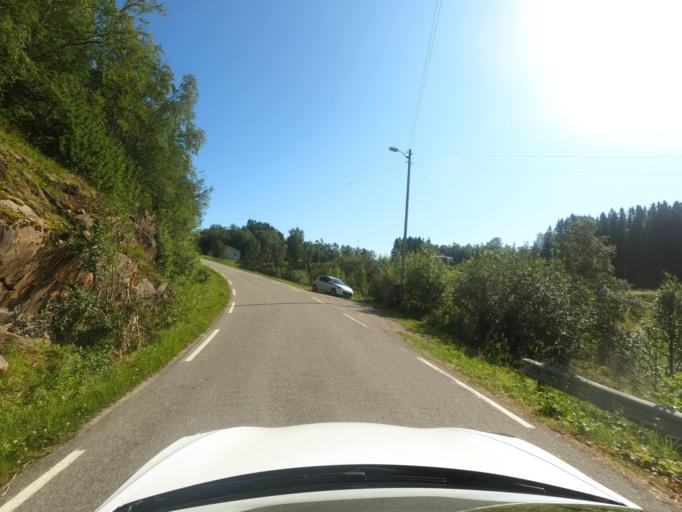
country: NO
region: Nordland
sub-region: Hadsel
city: Stokmarknes
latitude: 68.3045
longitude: 15.0706
